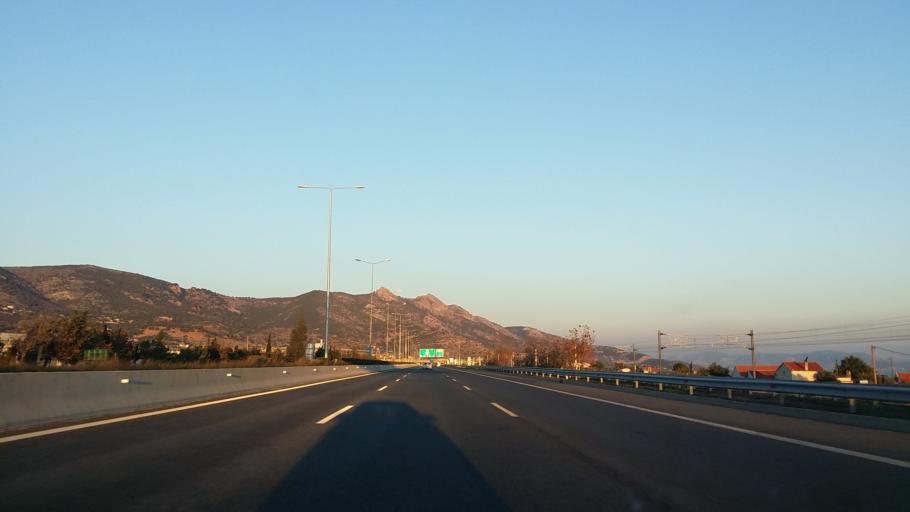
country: GR
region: Attica
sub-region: Nomarchia Dytikis Attikis
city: Nea Peramos
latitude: 38.0162
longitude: 23.4198
